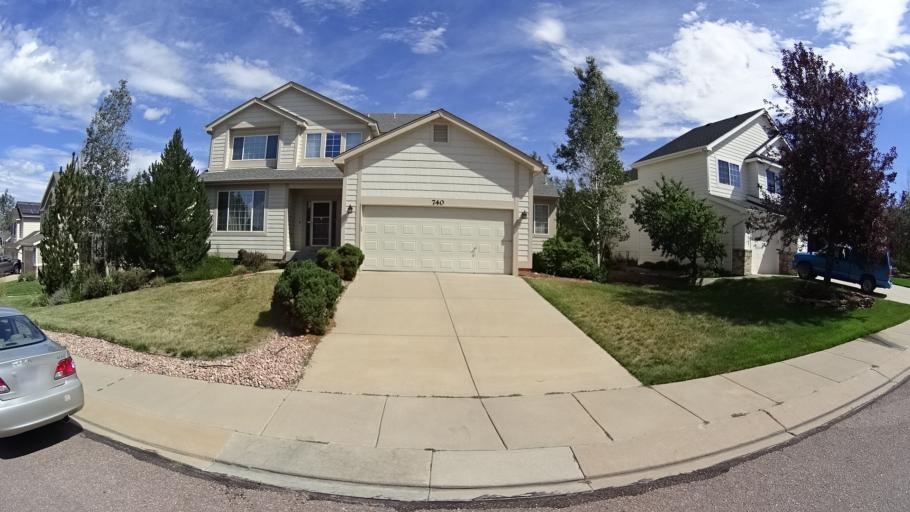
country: US
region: Colorado
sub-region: El Paso County
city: Gleneagle
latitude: 39.0279
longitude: -104.8158
